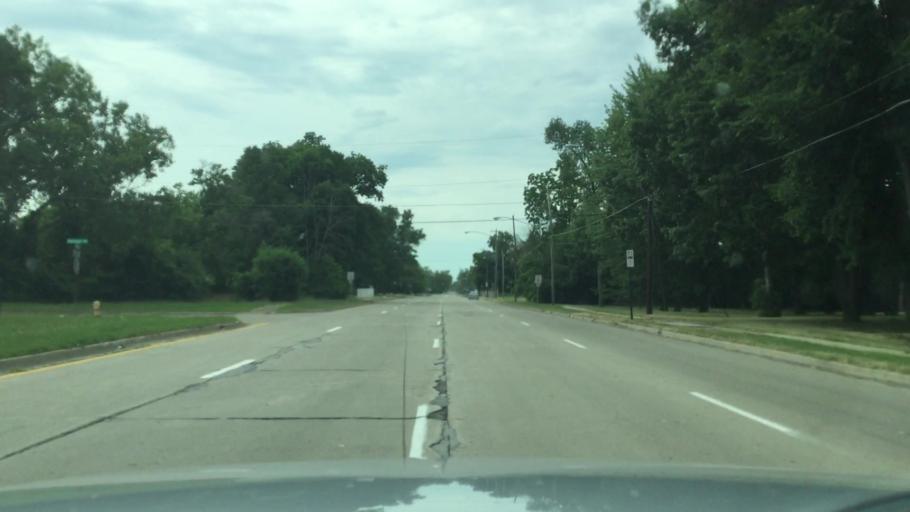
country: US
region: Michigan
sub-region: Genesee County
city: Beecher
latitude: 43.0659
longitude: -83.6845
